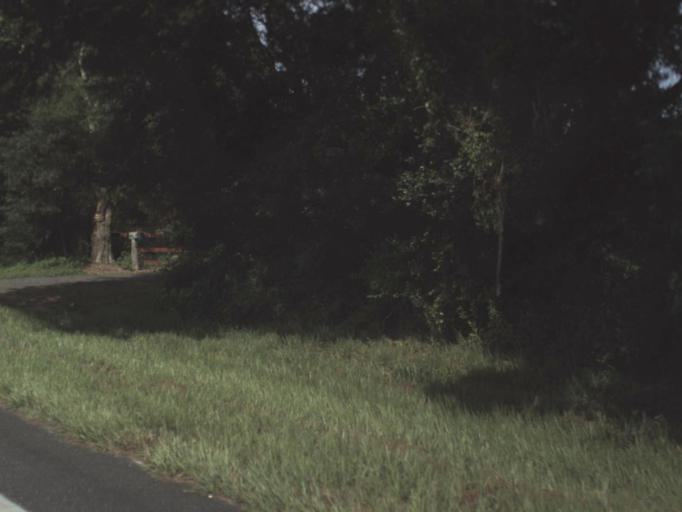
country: US
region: Florida
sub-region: Suwannee County
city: Live Oak
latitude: 30.2307
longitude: -83.0653
